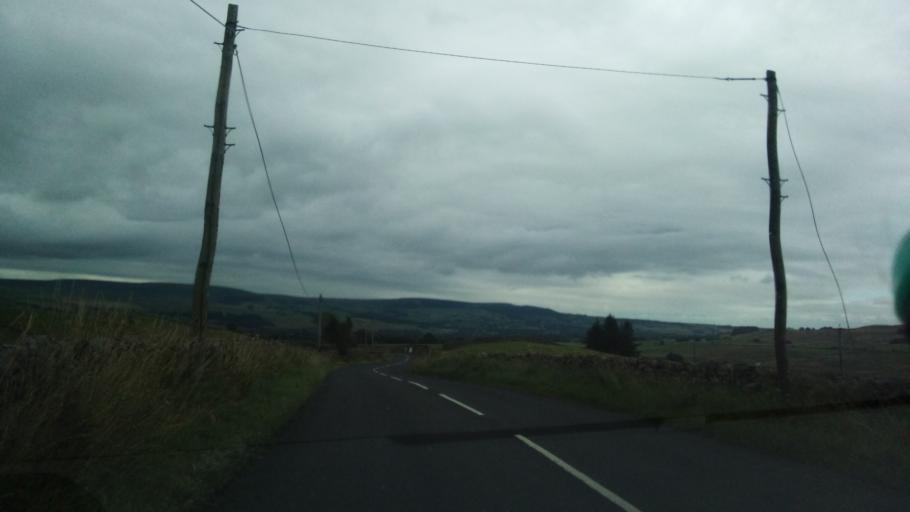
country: GB
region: England
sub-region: County Durham
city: Mickleton
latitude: 54.6067
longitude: -2.0955
